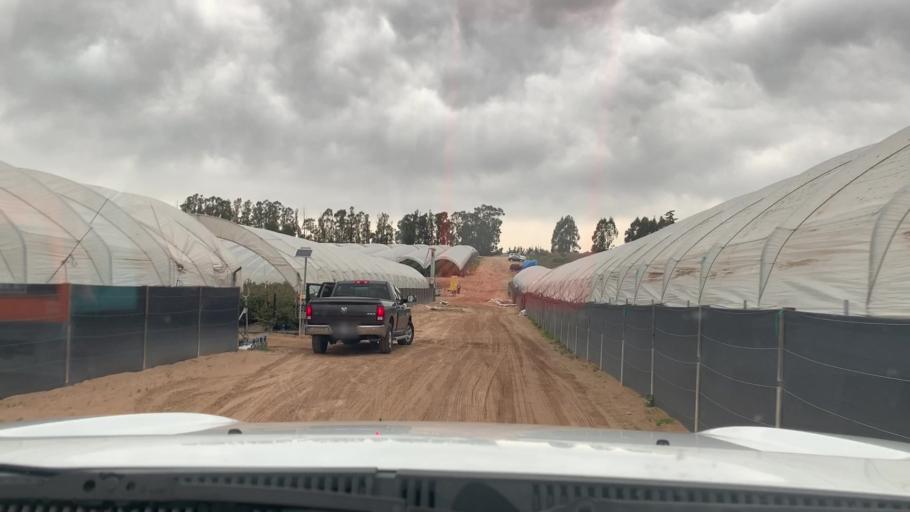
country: US
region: California
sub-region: San Luis Obispo County
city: Callender
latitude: 35.0633
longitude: -120.5675
